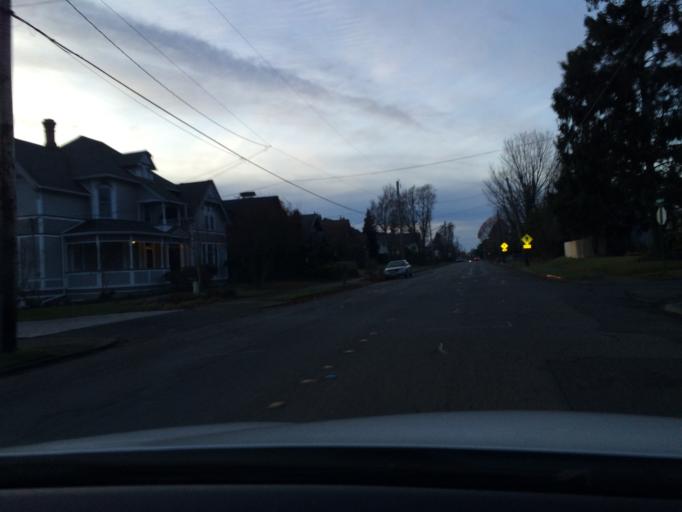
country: US
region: Washington
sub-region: Whatcom County
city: Bellingham
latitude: 48.7584
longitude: -122.4938
